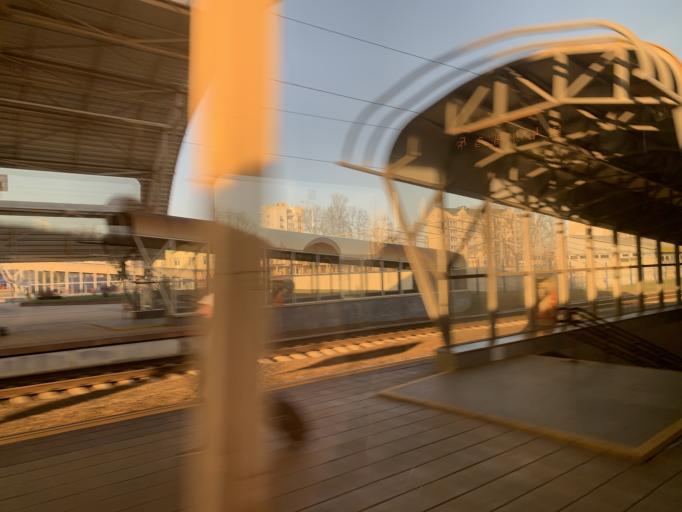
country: BY
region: Minsk
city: Zhdanovichy
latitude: 53.9470
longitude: 27.4269
